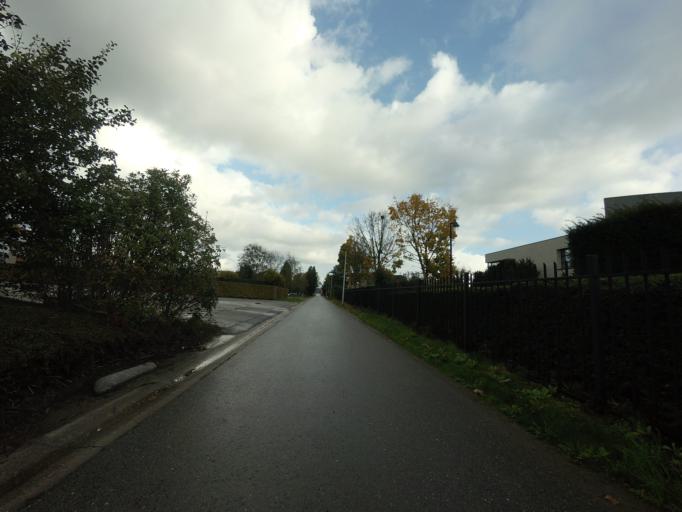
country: BE
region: Flanders
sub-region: Provincie Antwerpen
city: Aartselaar
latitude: 51.1312
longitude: 4.3710
